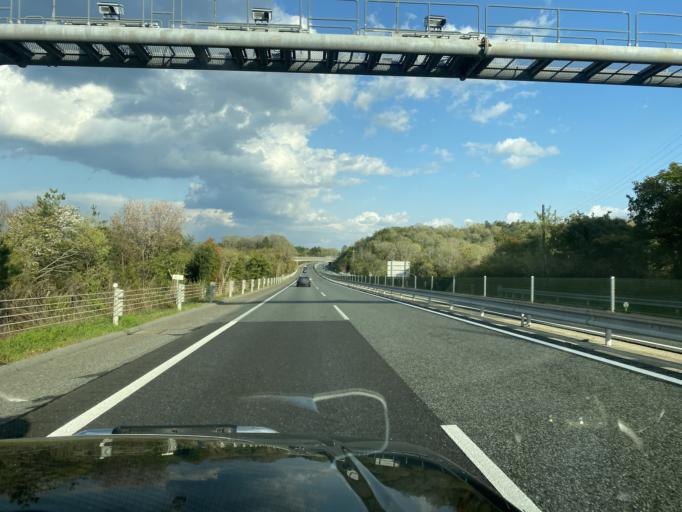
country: JP
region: Hyogo
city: Sandacho
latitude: 34.9441
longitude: 135.1488
